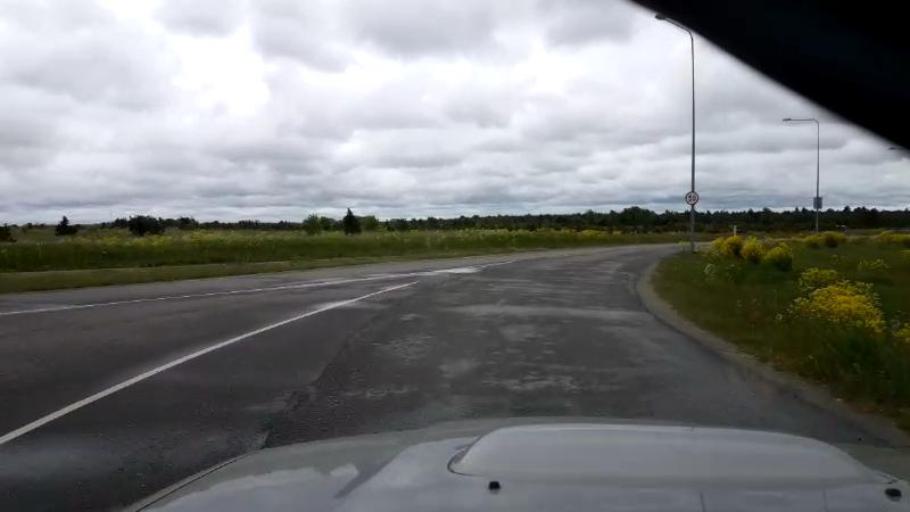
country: EE
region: Harju
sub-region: Harku vald
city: Tabasalu
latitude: 59.4550
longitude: 24.4579
